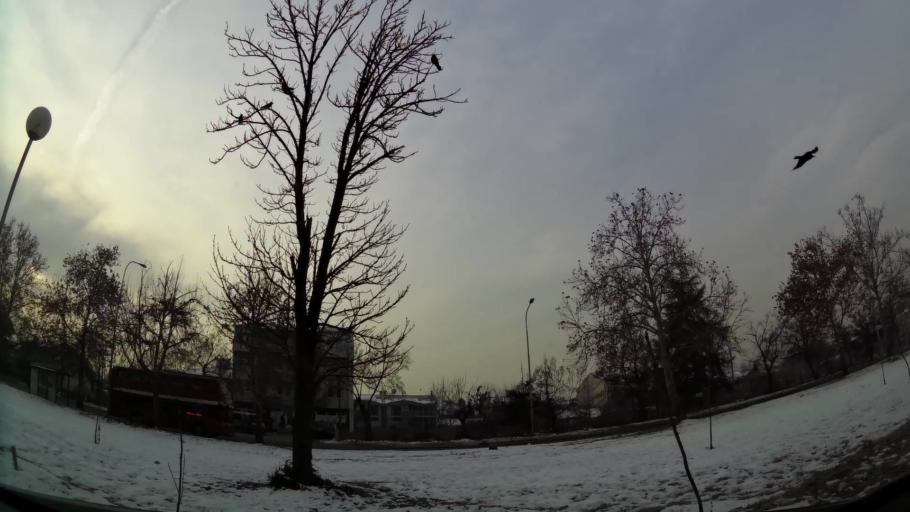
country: MK
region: Butel
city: Butel
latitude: 42.0249
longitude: 21.4478
